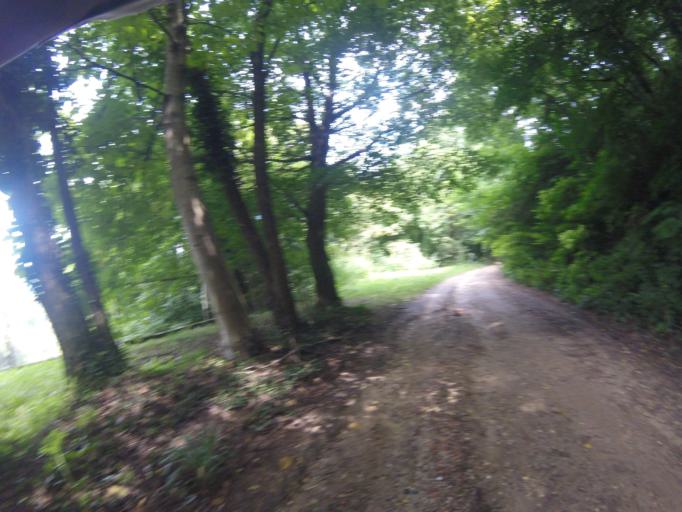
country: HU
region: Zala
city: Lenti
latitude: 46.5730
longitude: 16.6046
